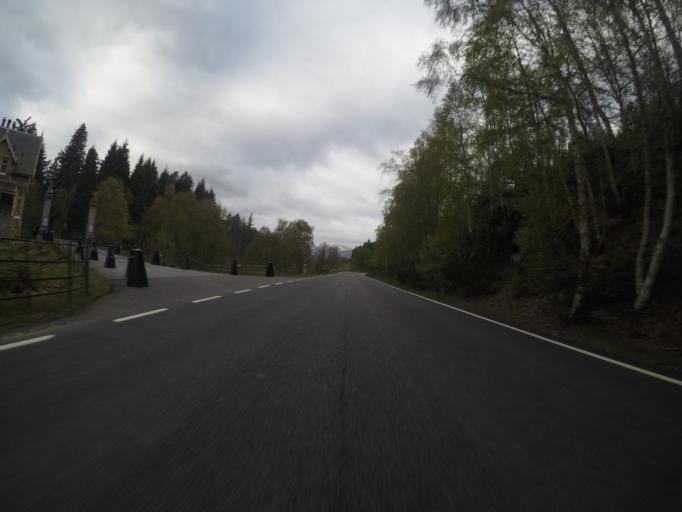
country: GB
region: Scotland
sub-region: Highland
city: Kingussie
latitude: 56.9757
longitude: -4.4047
